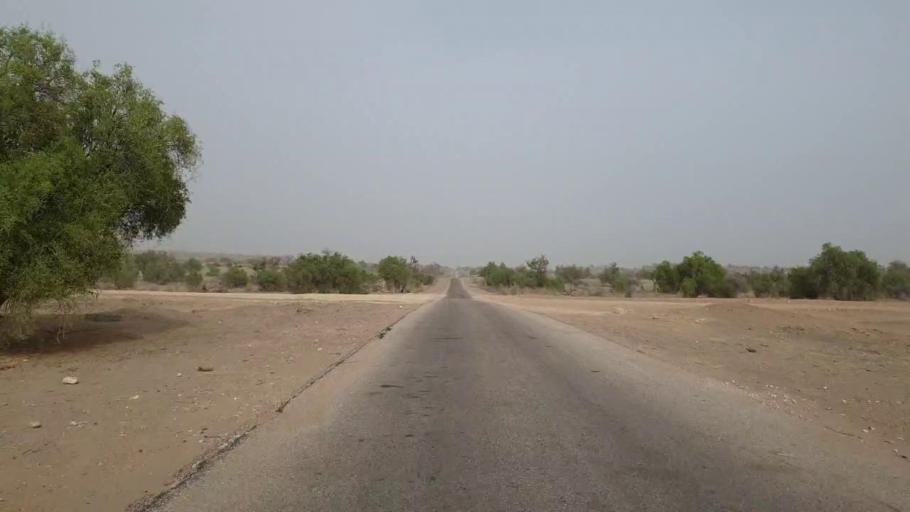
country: PK
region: Sindh
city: Islamkot
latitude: 24.5662
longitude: 70.3302
